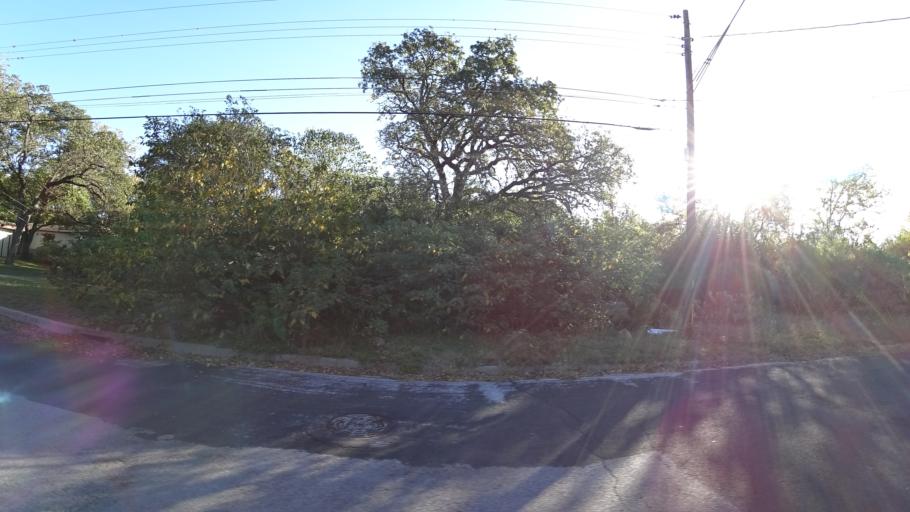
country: US
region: Texas
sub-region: Travis County
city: Austin
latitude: 30.2942
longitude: -97.6865
